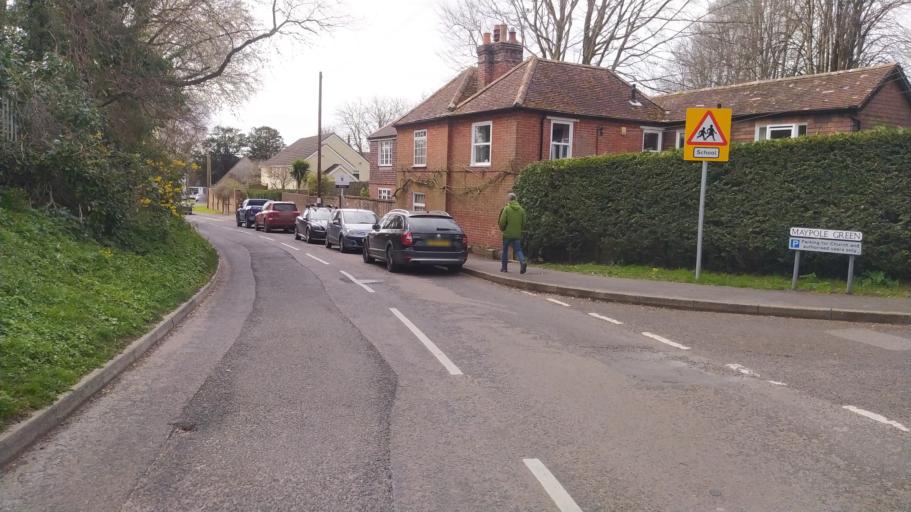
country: GB
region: England
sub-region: Hampshire
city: Bishops Waltham
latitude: 50.9559
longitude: -1.2088
